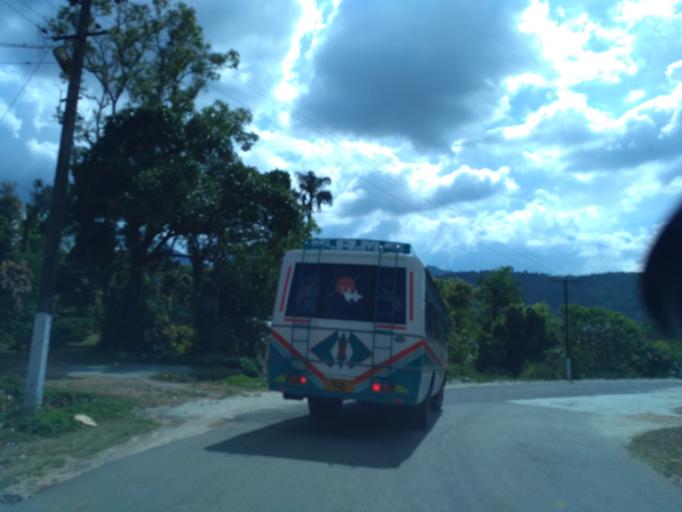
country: IN
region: Karnataka
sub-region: Kodagu
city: Madikeri
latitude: 12.3756
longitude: 75.5565
